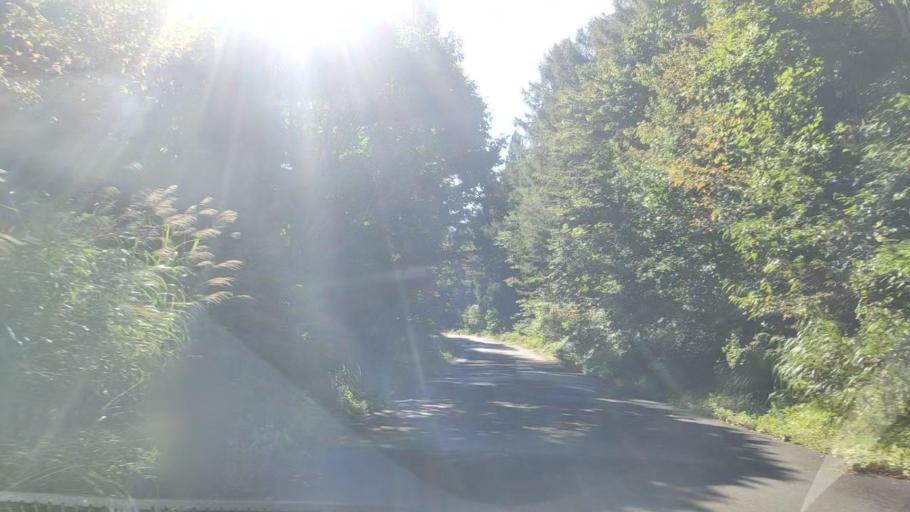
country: JP
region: Nagano
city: Iiyama
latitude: 36.8074
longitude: 138.4258
